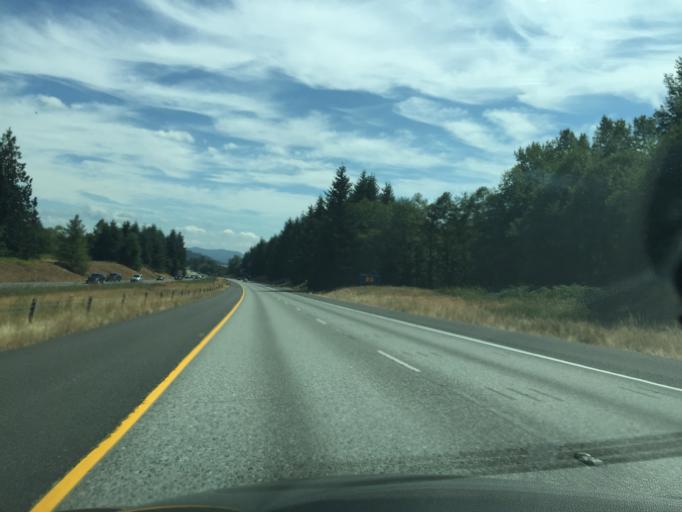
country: US
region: Washington
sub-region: Skagit County
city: Burlington
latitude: 48.5303
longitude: -122.3520
